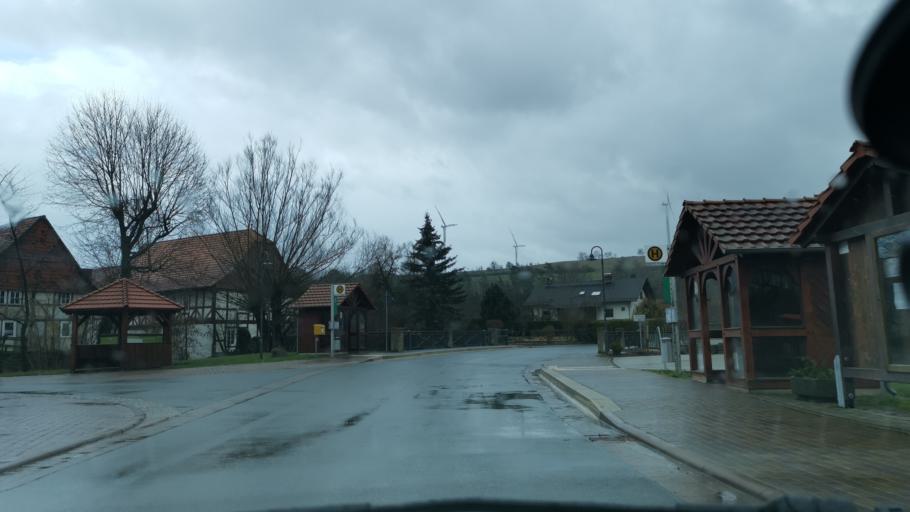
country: DE
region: Hesse
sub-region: Regierungsbezirk Kassel
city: Cornberg
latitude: 51.0586
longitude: 9.8849
